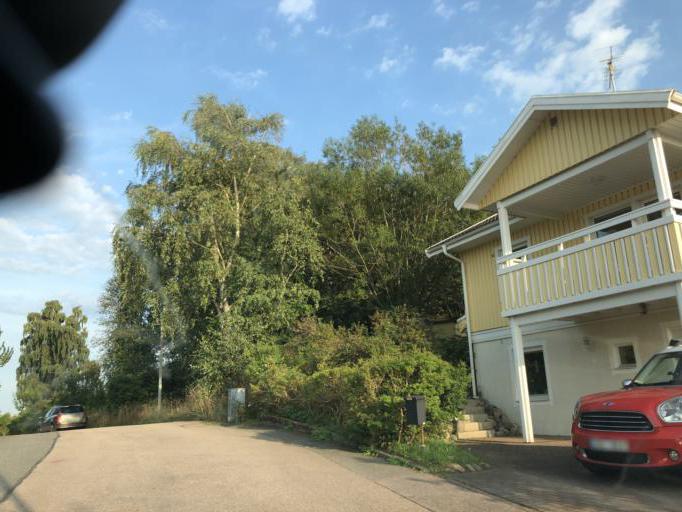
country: SE
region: Vaestra Goetaland
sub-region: Goteborg
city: Goeteborg
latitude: 57.7357
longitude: 11.9771
